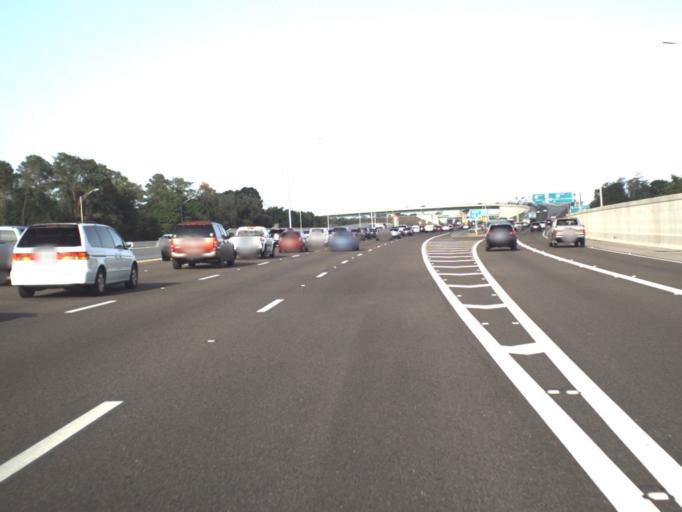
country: US
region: Florida
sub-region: Orange County
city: Union Park
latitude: 28.5471
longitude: -81.2697
